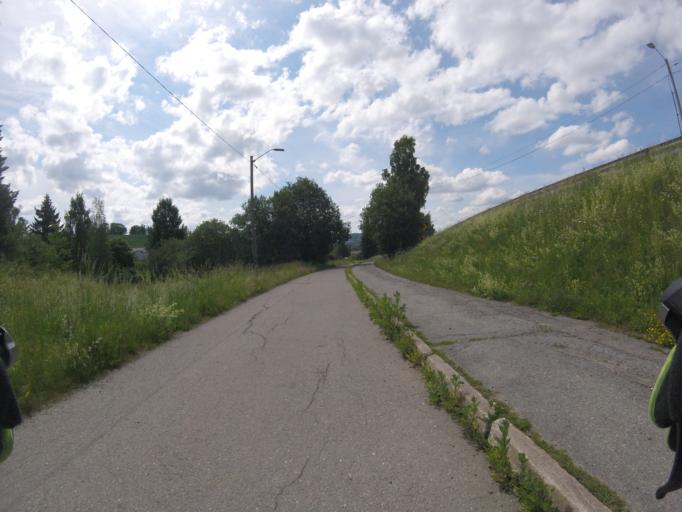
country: NO
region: Akershus
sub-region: Skedsmo
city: Lillestrom
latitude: 59.9725
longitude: 11.0552
